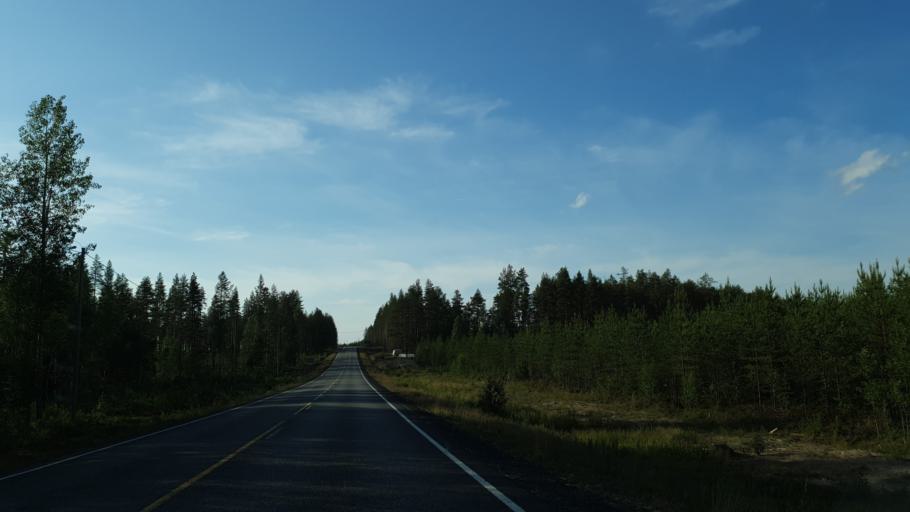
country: FI
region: Kainuu
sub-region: Kehys-Kainuu
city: Kuhmo
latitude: 64.0934
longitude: 29.4791
